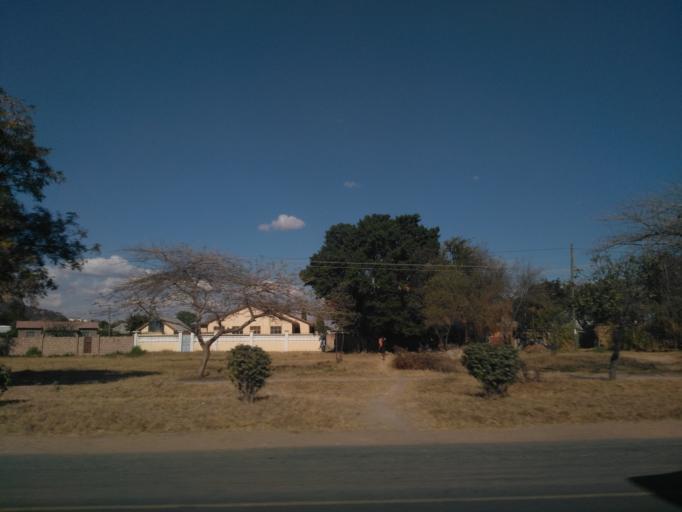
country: TZ
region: Dodoma
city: Dodoma
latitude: -6.1620
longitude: 35.7468
